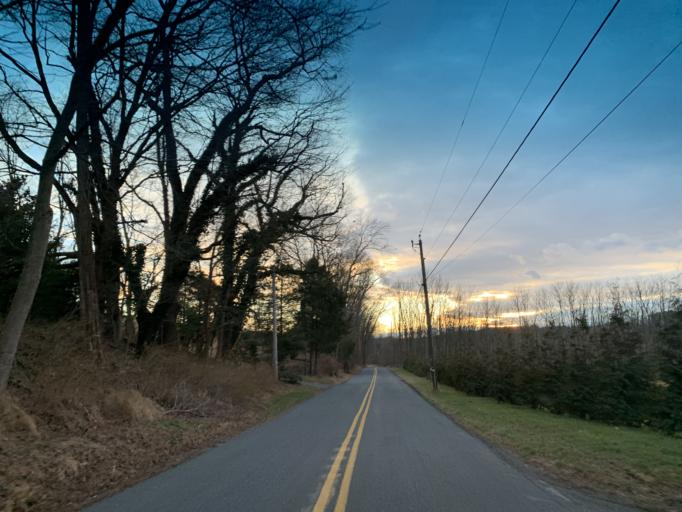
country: US
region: Maryland
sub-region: Harford County
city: Bel Air North
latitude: 39.6188
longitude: -76.3114
